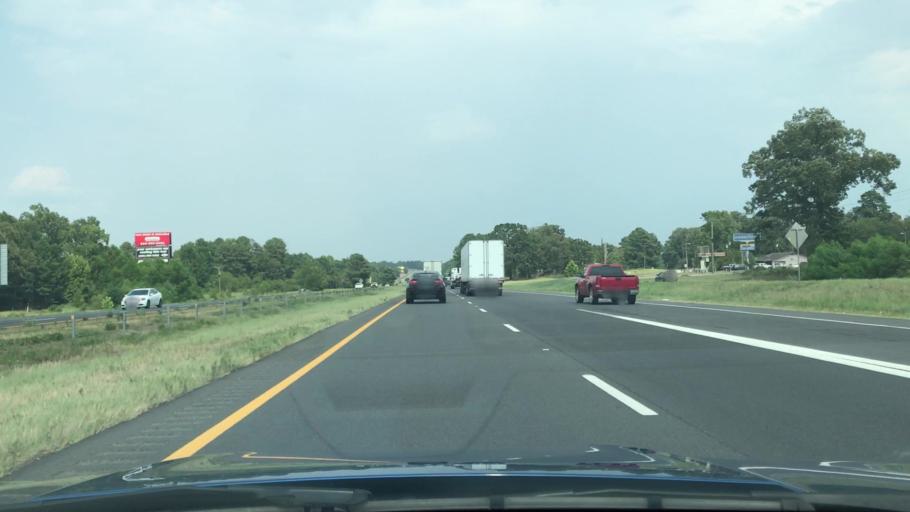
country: US
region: Texas
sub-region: Gregg County
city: Longview
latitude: 32.4606
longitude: -94.6633
